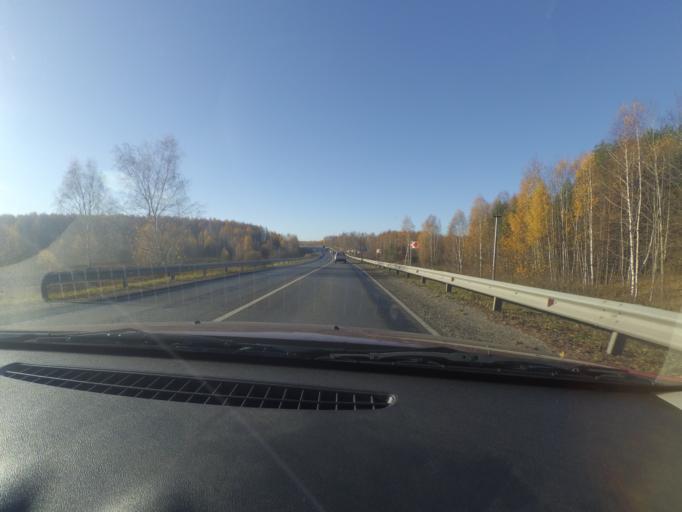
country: RU
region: Nizjnij Novgorod
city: Bogorodsk
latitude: 56.1276
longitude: 43.6015
